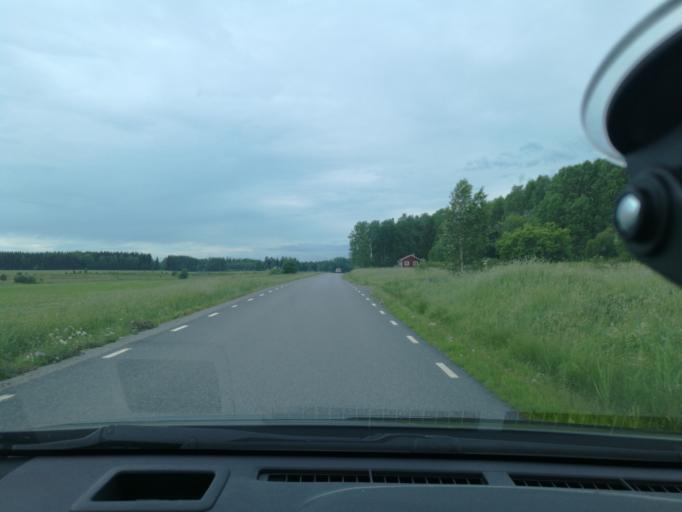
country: SE
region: Vaestmanland
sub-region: Surahammars Kommun
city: Ramnas
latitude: 59.8412
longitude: 16.3137
